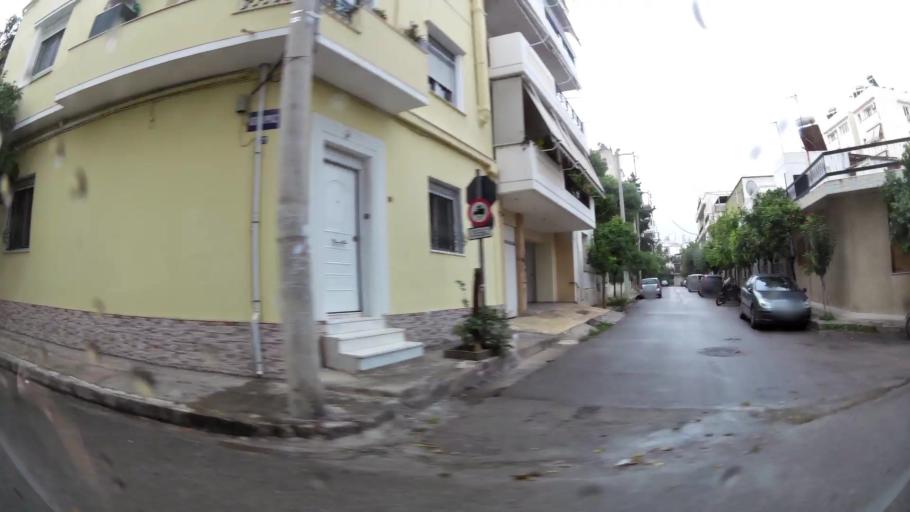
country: GR
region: Attica
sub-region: Nomarchia Athinas
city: Ymittos
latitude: 37.9556
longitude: 23.7508
